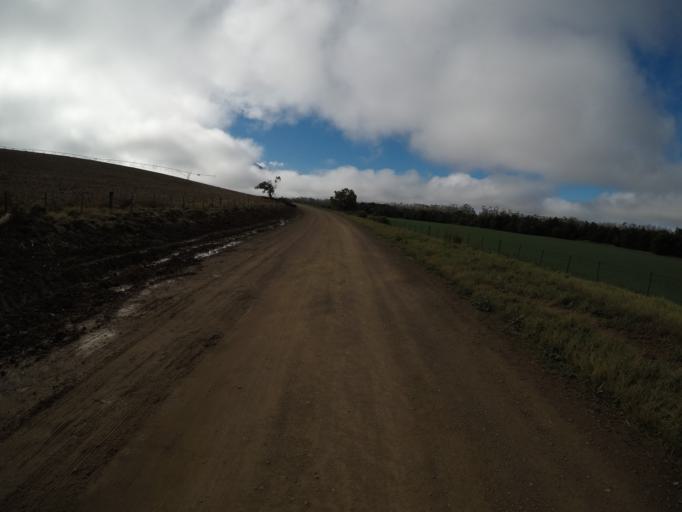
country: ZA
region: Western Cape
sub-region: Overberg District Municipality
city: Caledon
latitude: -34.1170
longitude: 19.7880
